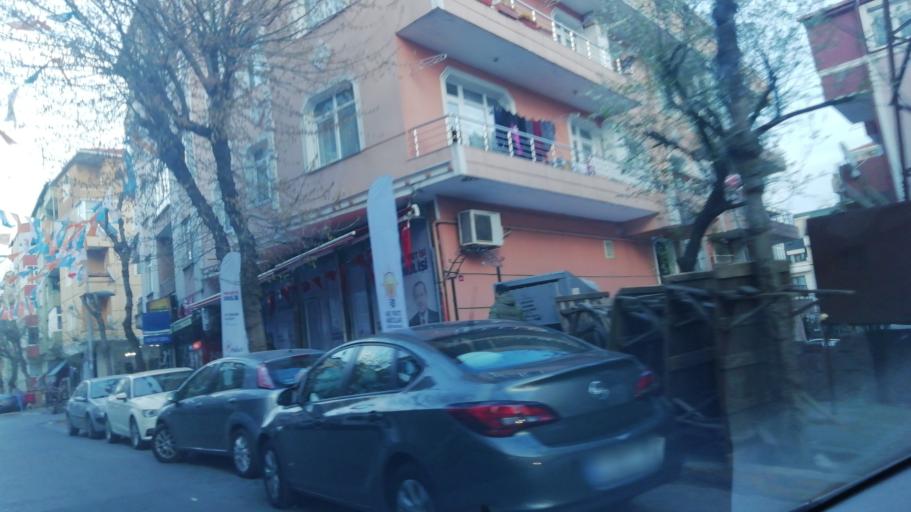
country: TR
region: Istanbul
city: Yakuplu
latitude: 40.9764
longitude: 28.7351
